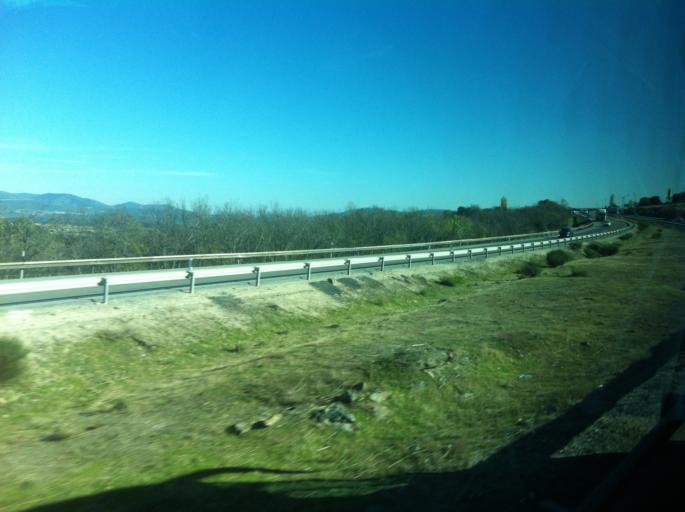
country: ES
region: Madrid
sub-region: Provincia de Madrid
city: Buitrago del Lozoya
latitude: 40.9468
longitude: -3.6386
